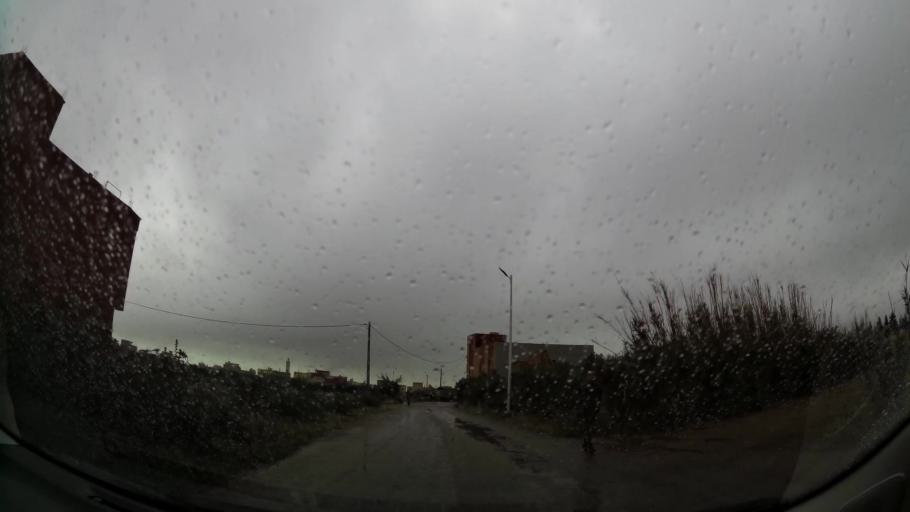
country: MA
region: Oriental
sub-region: Nador
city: Nador
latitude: 35.1529
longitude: -2.9698
